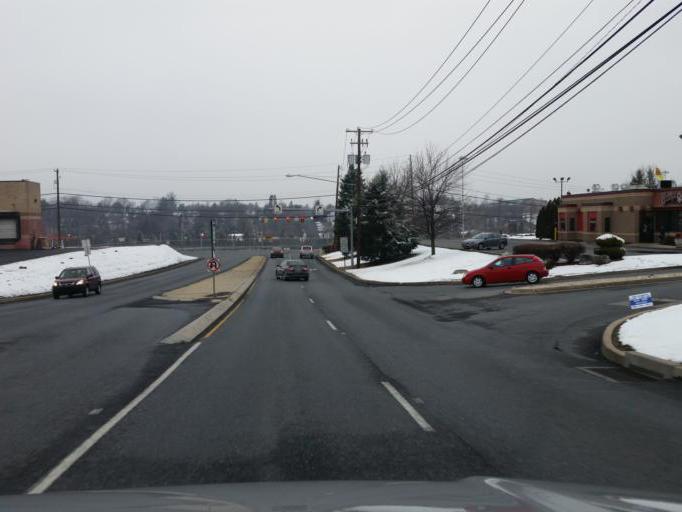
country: US
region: Pennsylvania
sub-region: Dauphin County
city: Rutherford
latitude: 40.2607
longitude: -76.7755
